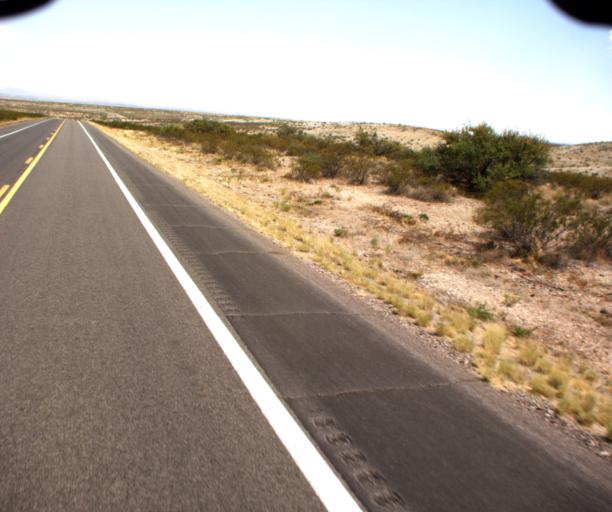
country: US
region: Arizona
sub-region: Greenlee County
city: Clifton
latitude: 32.7294
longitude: -109.1836
